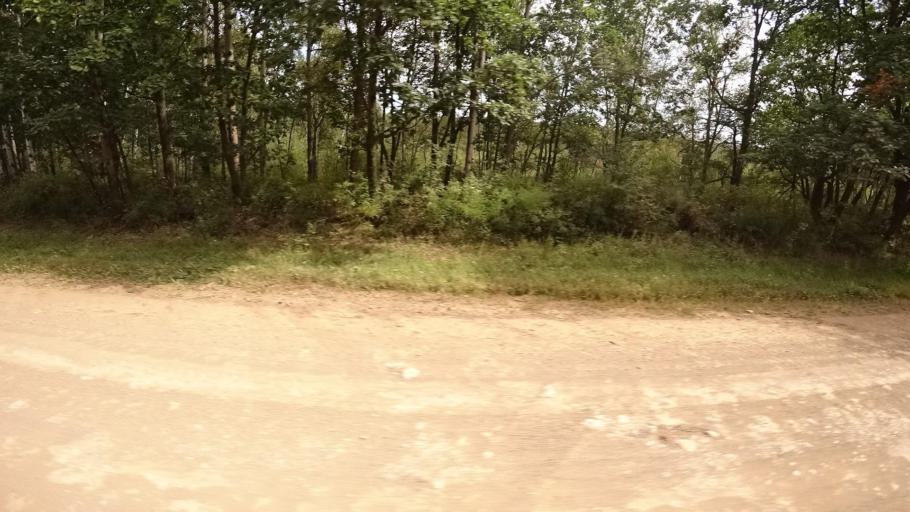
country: RU
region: Primorskiy
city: Yakovlevka
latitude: 44.4939
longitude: 133.5877
